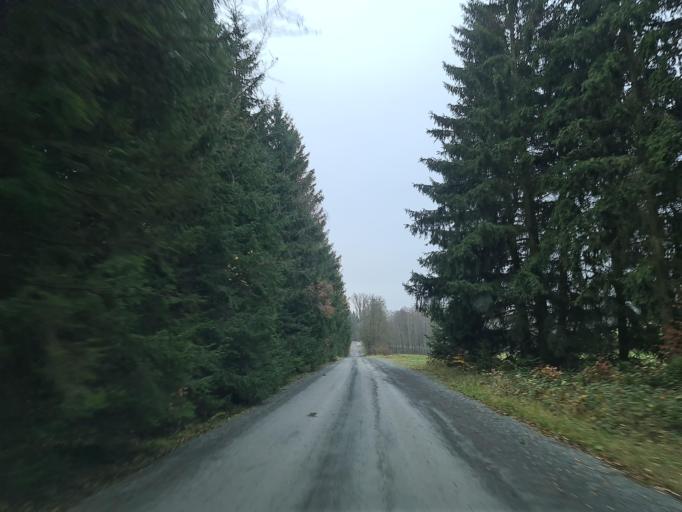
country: DE
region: Saxony
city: Mehltheuer
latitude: 50.5199
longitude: 12.0448
